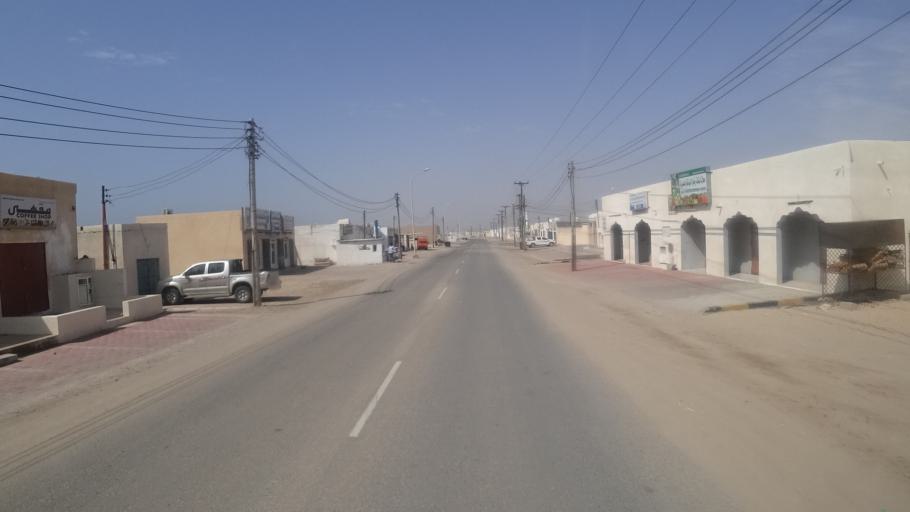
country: OM
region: Ash Sharqiyah
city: Sur
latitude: 22.1189
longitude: 59.7165
